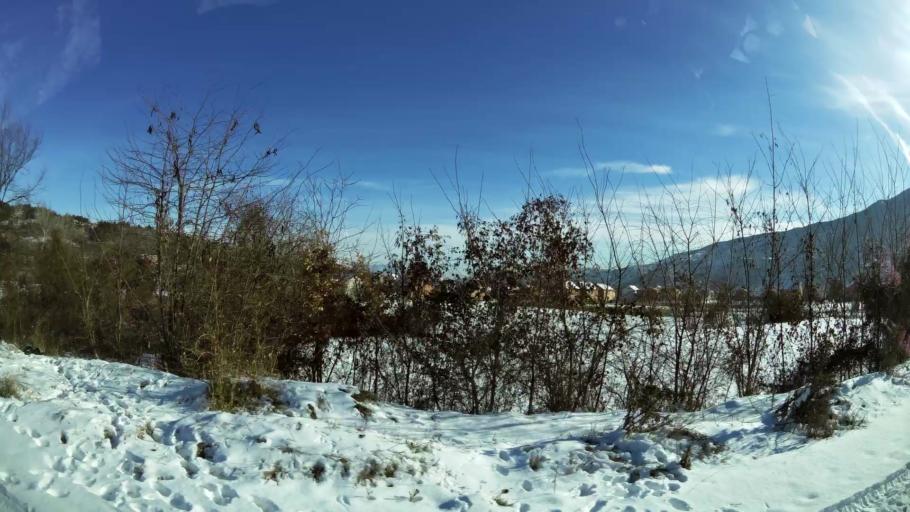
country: MK
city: Ljubin
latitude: 41.9823
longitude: 21.3003
